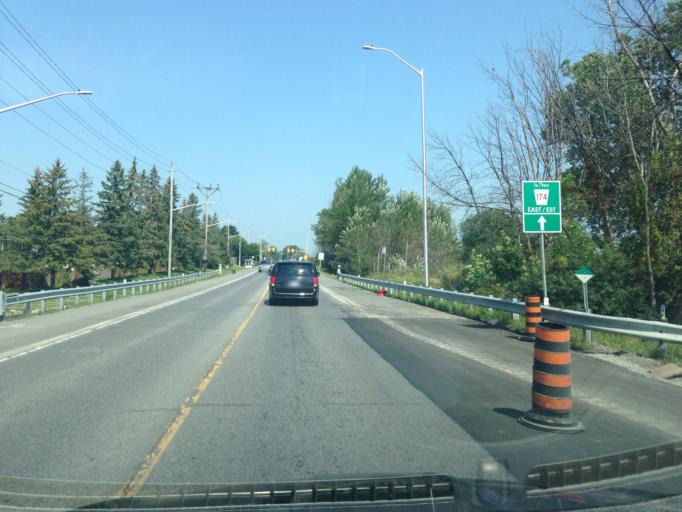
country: CA
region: Ontario
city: Ottawa
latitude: 45.4212
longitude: -75.5967
